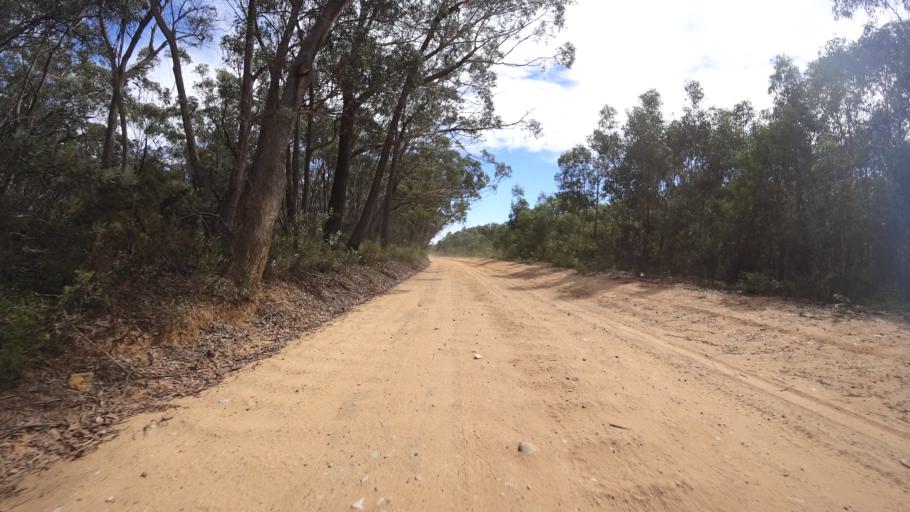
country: AU
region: New South Wales
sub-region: Lithgow
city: Lithgow
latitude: -33.3340
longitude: 150.2495
